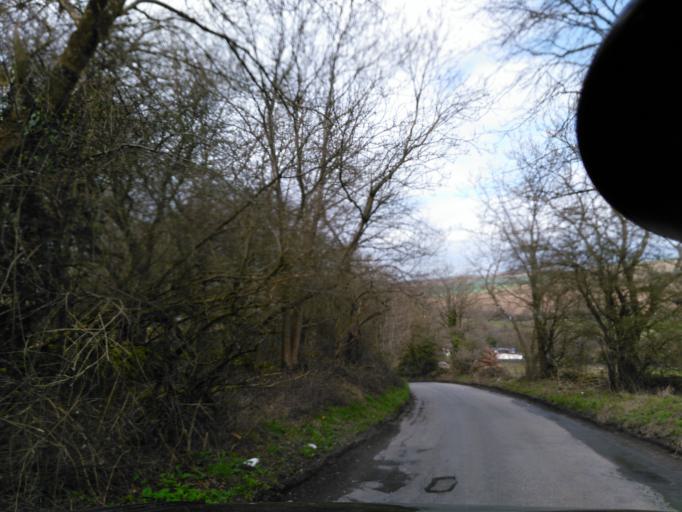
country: GB
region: England
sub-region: Gloucestershire
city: Charlton Kings
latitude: 51.8226
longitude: -2.0475
